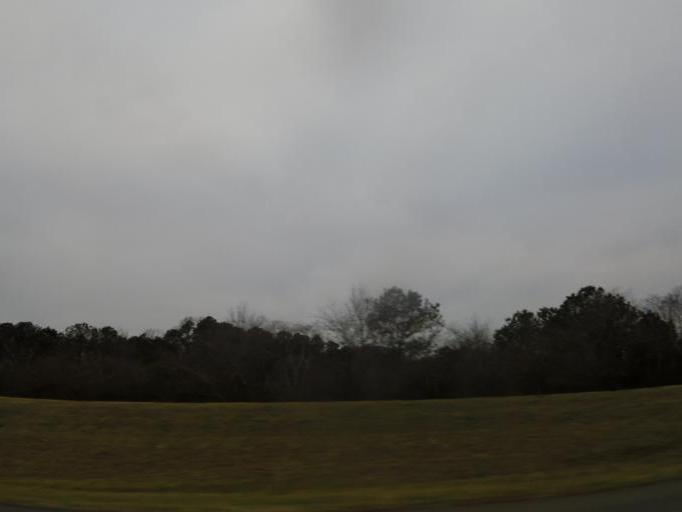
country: US
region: Alabama
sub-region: Jefferson County
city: Gardendale
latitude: 33.6757
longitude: -86.8290
